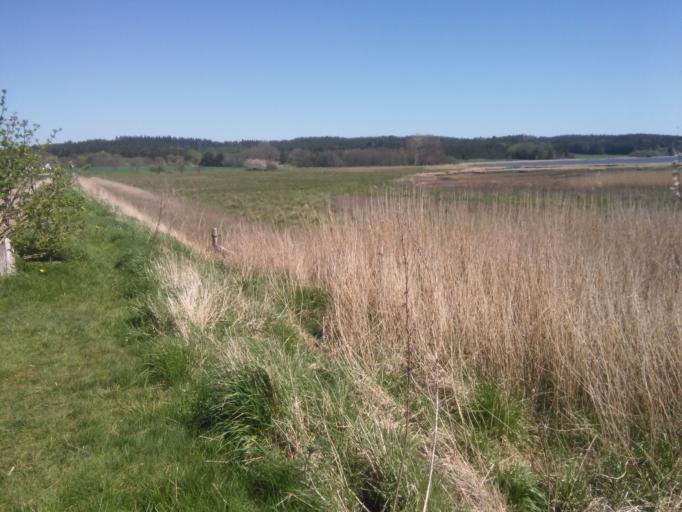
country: DK
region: Central Jutland
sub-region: Odder Kommune
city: Odder
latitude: 55.8808
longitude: 10.0641
